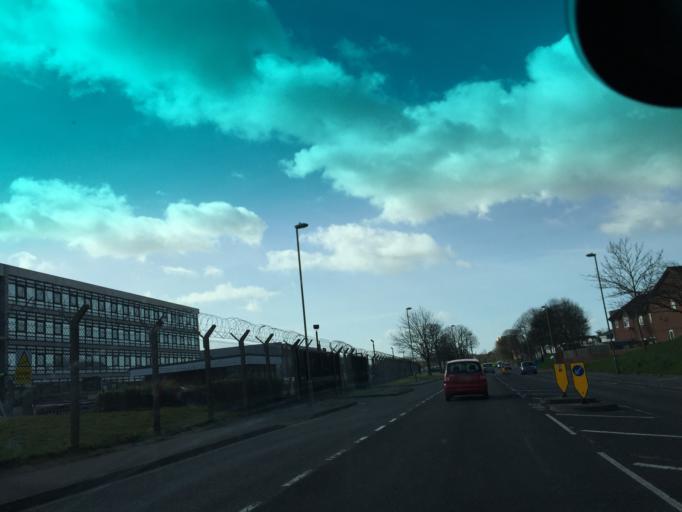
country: GB
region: England
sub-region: Hampshire
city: Gosport
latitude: 50.8092
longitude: -1.1631
